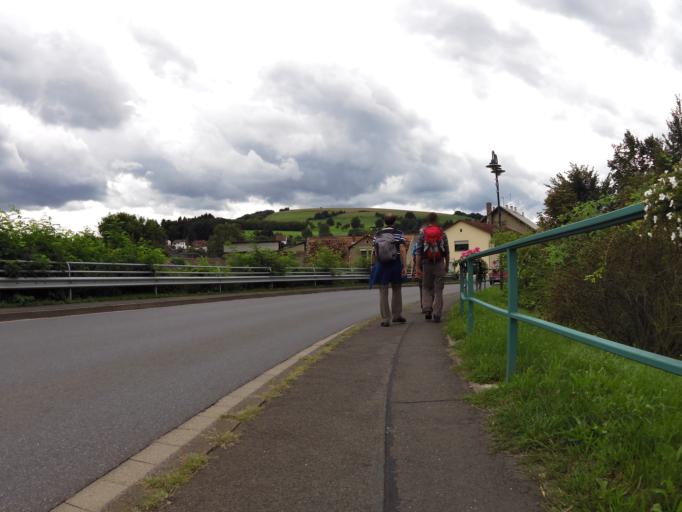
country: DE
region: Rheinland-Pfalz
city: Staudernheim
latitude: 49.7781
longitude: 7.6906
